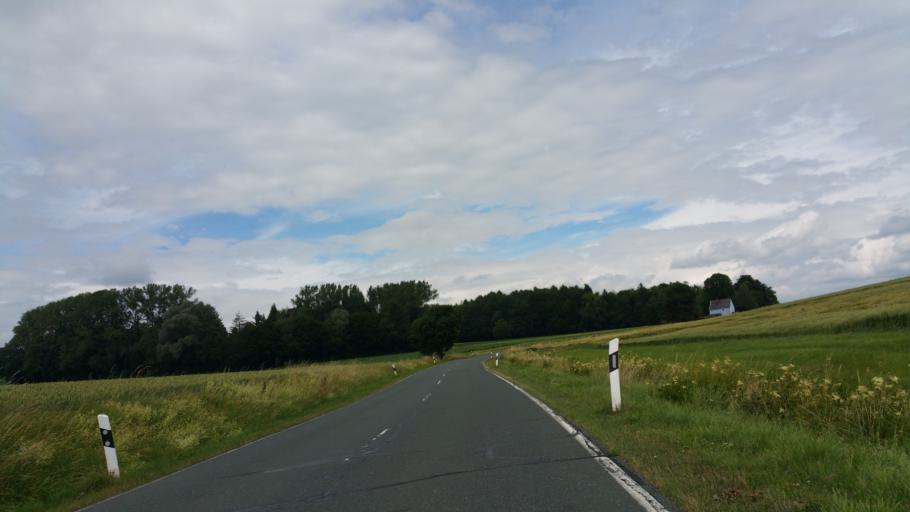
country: DE
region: Bavaria
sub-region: Upper Franconia
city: Schwarzenbach an der Saale
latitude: 50.2186
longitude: 11.9179
